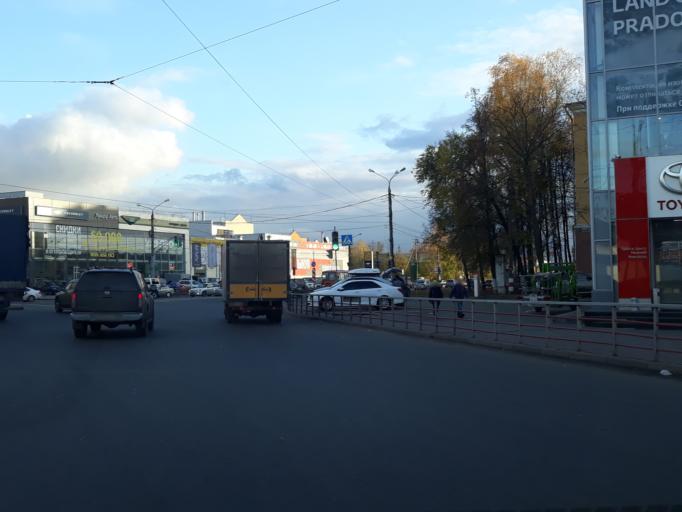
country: RU
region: Nizjnij Novgorod
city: Nizhniy Novgorod
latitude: 56.3143
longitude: 43.8984
